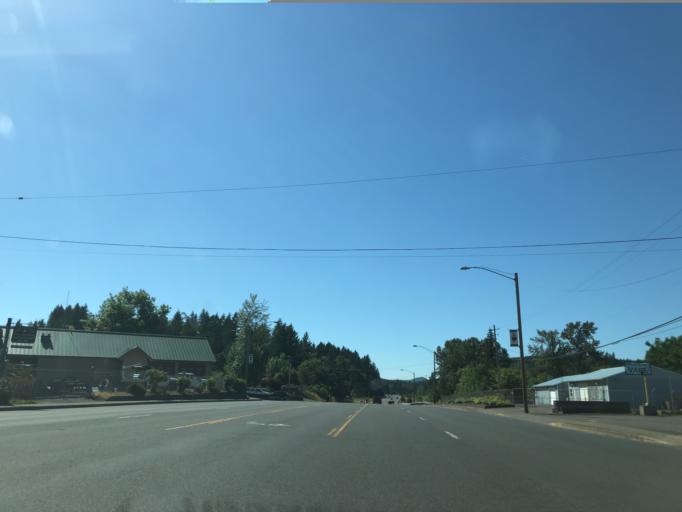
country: US
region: Oregon
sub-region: Linn County
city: Sweet Home
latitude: 44.3995
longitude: -122.7408
